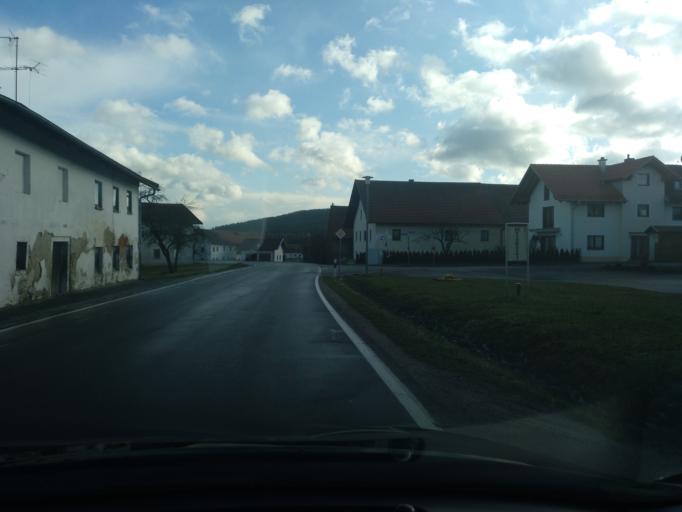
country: DE
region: Bavaria
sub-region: Lower Bavaria
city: Konzell
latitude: 49.1037
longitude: 12.7198
